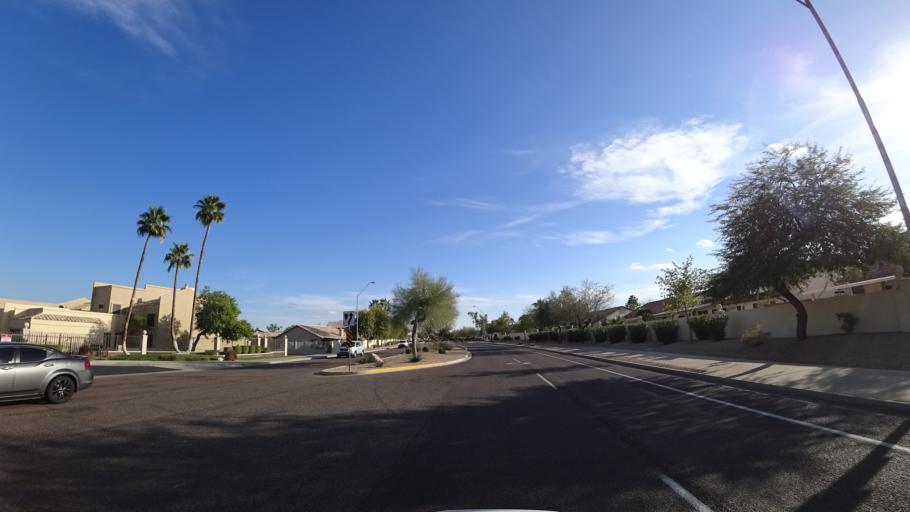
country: US
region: Arizona
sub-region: Maricopa County
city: Sun City
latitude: 33.6202
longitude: -112.2552
